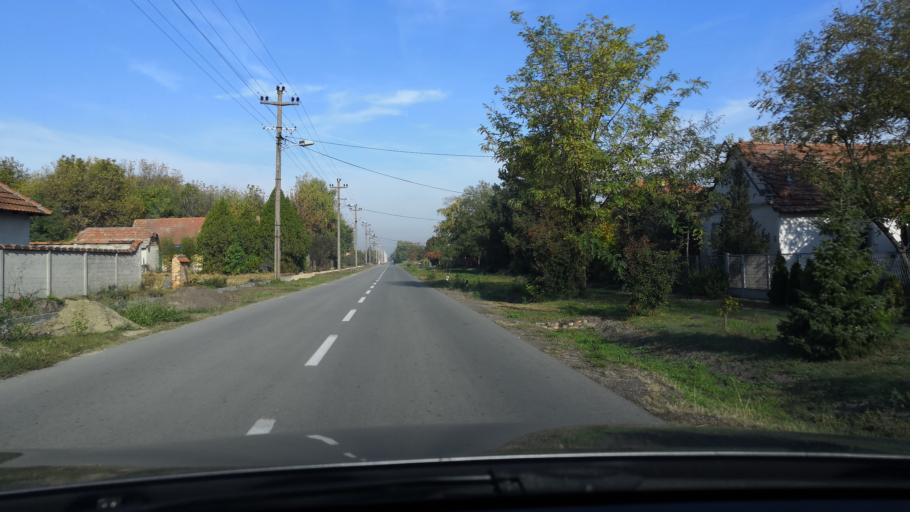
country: HU
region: Csongrad
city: Morahalom
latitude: 46.1313
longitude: 19.8548
